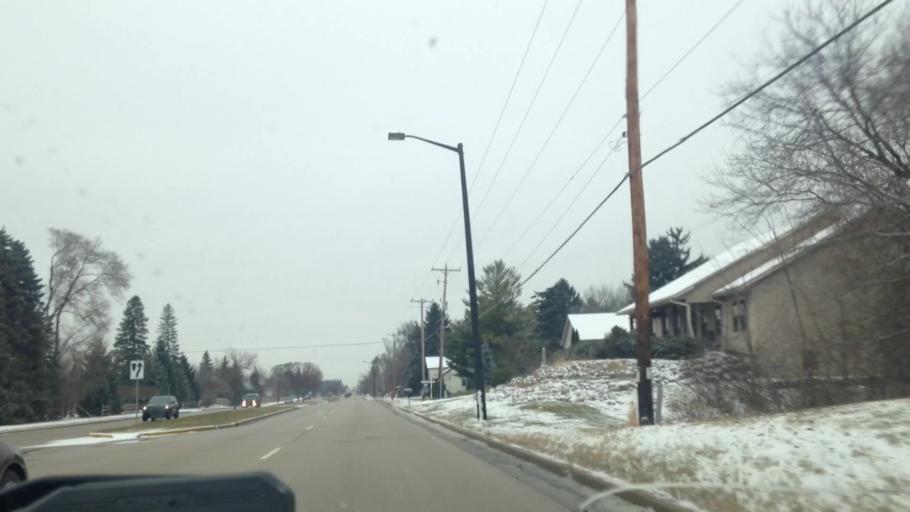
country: US
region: Wisconsin
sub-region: Waukesha County
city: Butler
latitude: 43.1110
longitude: -88.1054
